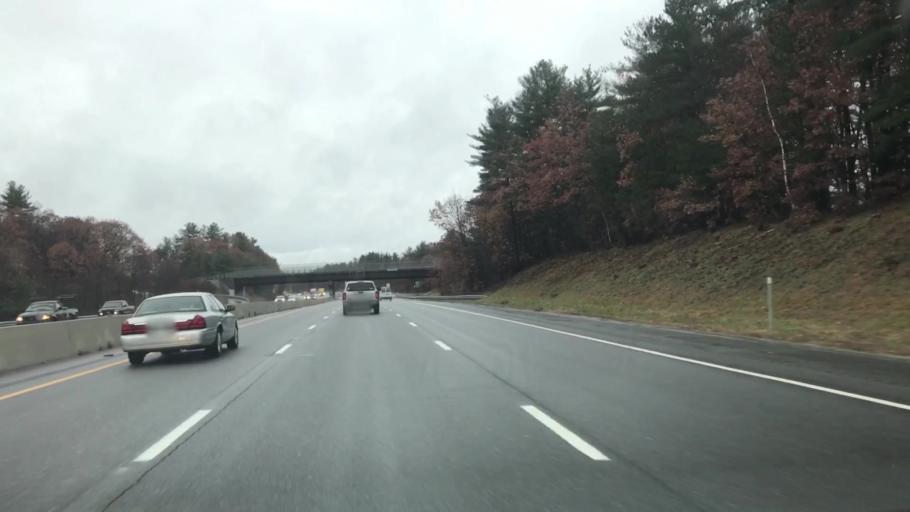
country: US
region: New Hampshire
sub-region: Merrimack County
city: Hooksett
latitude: 43.1001
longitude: -71.4752
